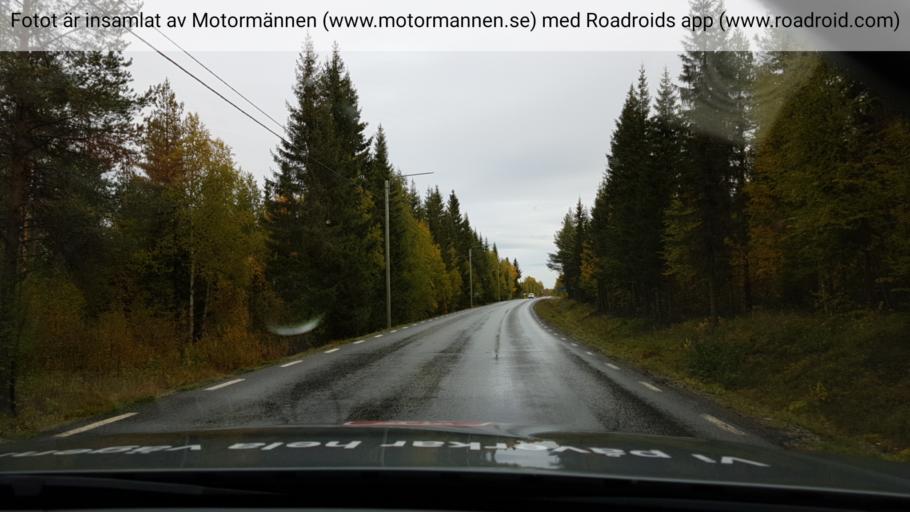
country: SE
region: Vaesterbotten
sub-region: Vilhelmina Kommun
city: Sjoberg
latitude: 64.6518
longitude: 16.3276
